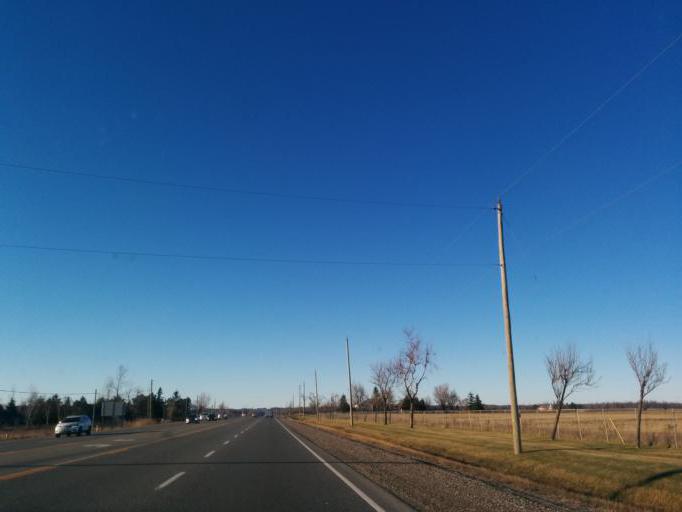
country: CA
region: Ontario
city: Brampton
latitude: 43.7810
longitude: -79.8883
